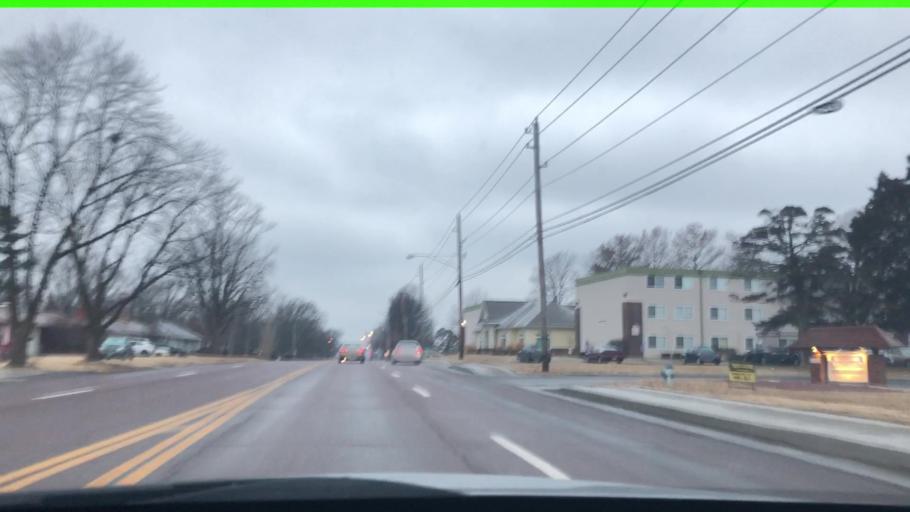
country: US
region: Missouri
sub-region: Boone County
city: Columbia
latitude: 38.9542
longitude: -92.3741
